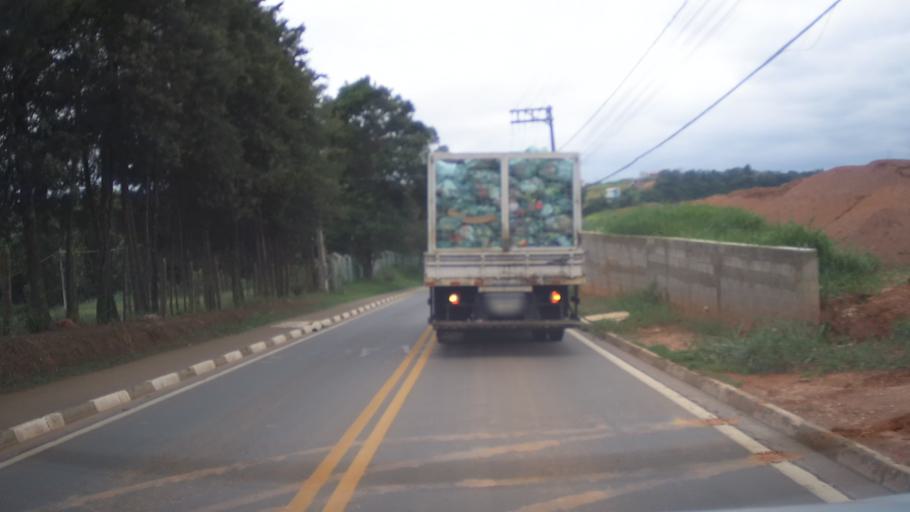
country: BR
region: Sao Paulo
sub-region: Louveira
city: Louveira
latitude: -23.0784
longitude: -46.9657
